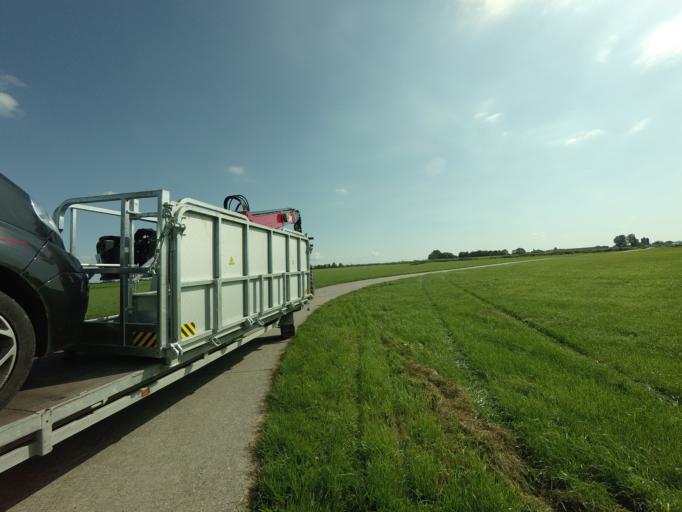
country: NL
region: Friesland
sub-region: Gemeente Littenseradiel
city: Makkum
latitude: 53.0891
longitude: 5.6350
